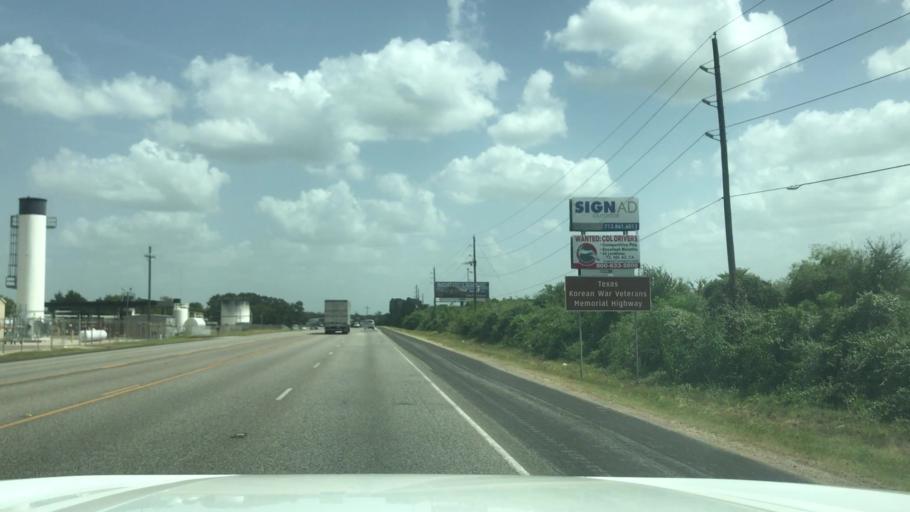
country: US
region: Texas
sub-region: Robertson County
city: Hearne
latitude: 30.8637
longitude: -96.5819
